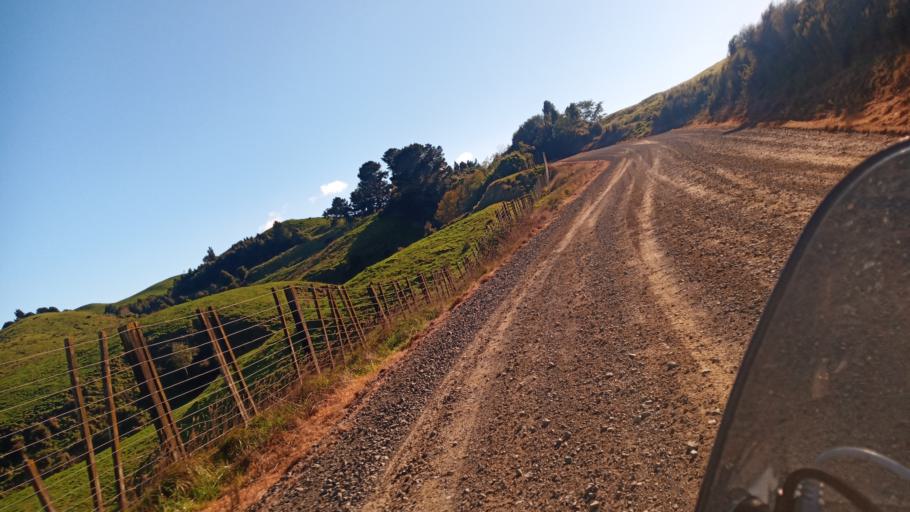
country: NZ
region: Hawke's Bay
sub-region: Wairoa District
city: Wairoa
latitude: -38.7987
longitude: 177.2859
